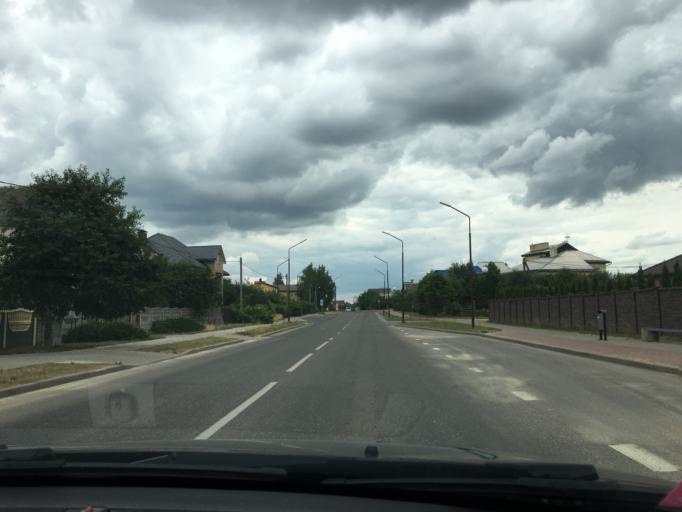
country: BY
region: Grodnenskaya
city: Hrodna
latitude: 53.6222
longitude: 23.8401
